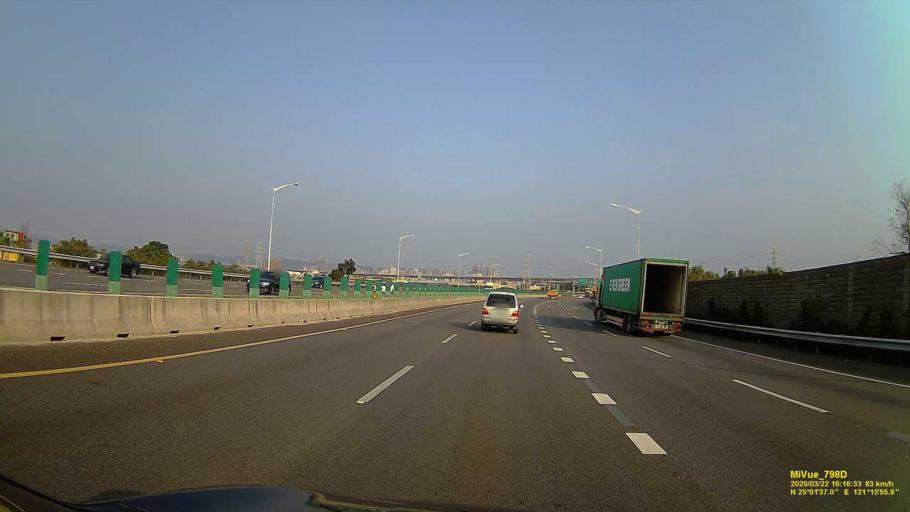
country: TW
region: Taiwan
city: Taoyuan City
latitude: 25.0263
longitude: 121.2660
